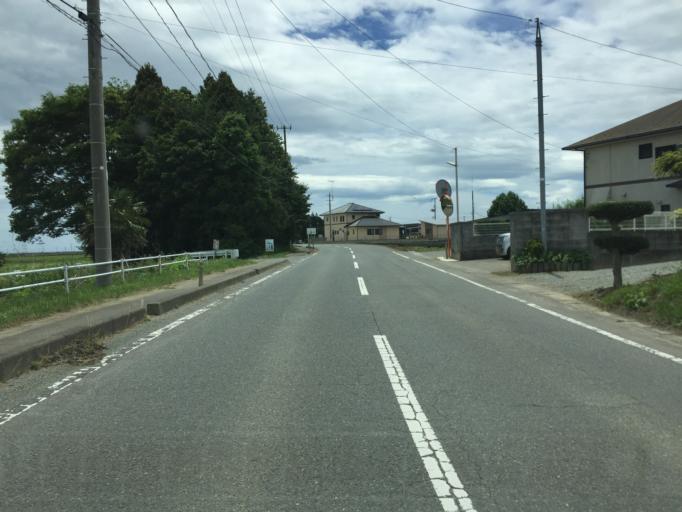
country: JP
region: Fukushima
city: Namie
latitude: 37.6343
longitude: 141.0008
